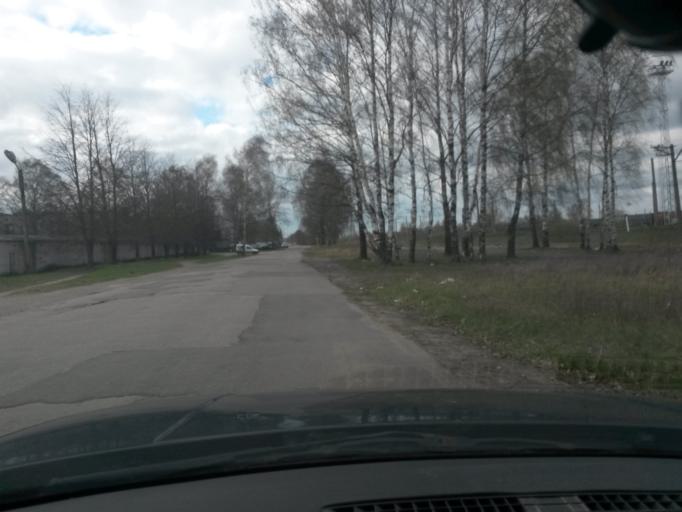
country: LV
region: Kekava
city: Kekava
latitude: 56.8997
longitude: 24.2199
